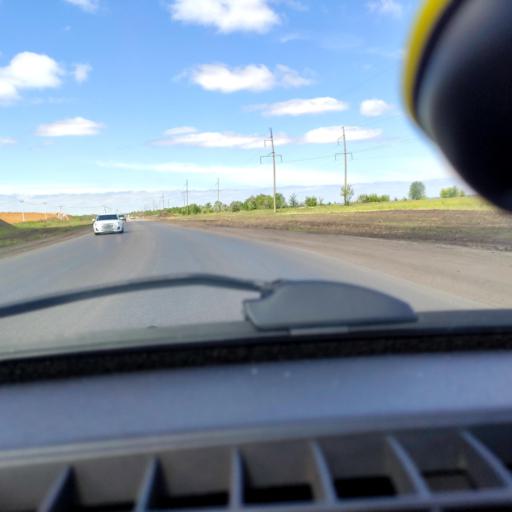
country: RU
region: Samara
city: Podstepki
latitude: 53.5617
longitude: 49.1981
